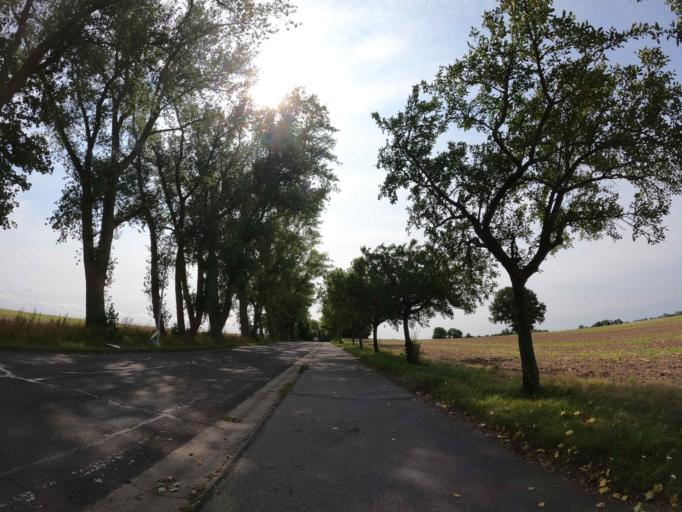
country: DE
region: Mecklenburg-Vorpommern
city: Kramerhof
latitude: 54.3474
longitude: 13.0691
